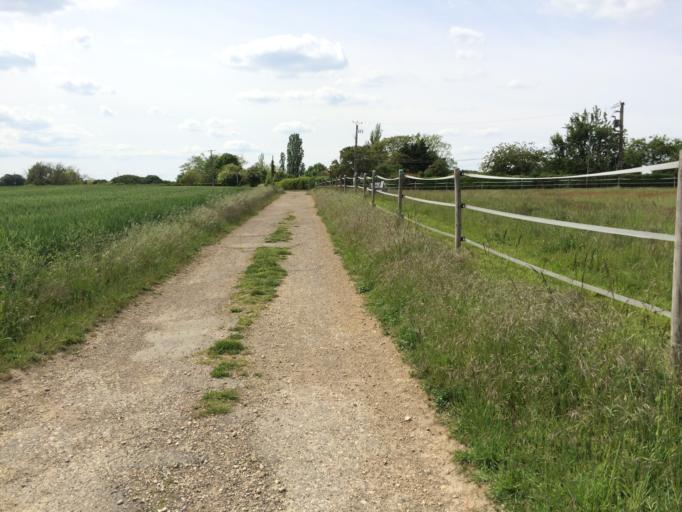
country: FR
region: Ile-de-France
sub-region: Departement de l'Essonne
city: Vauhallan
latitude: 48.7273
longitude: 2.2116
